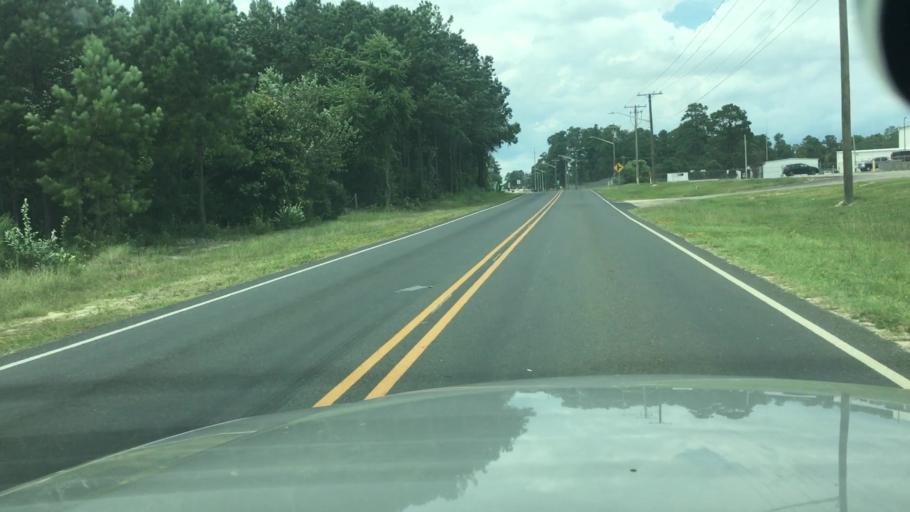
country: US
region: North Carolina
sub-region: Cumberland County
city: Hope Mills
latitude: 34.9891
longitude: -78.8906
